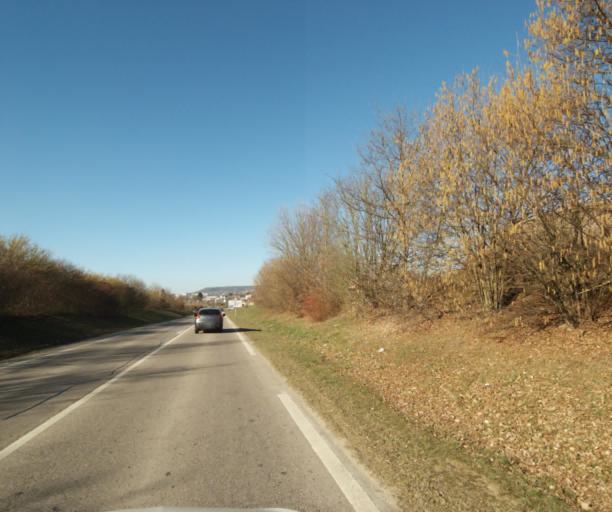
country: FR
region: Lorraine
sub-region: Departement de Meurthe-et-Moselle
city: Tomblaine
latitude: 48.6816
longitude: 6.2231
